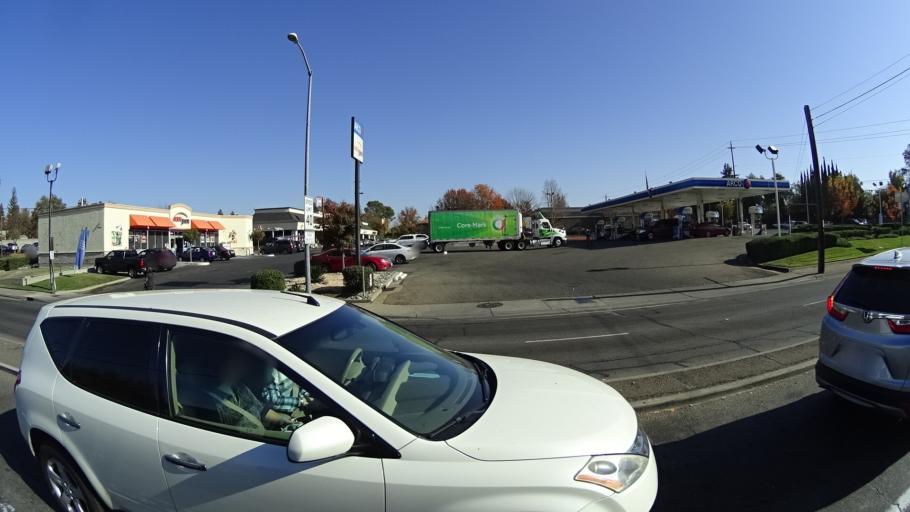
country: US
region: California
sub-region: Sacramento County
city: Fair Oaks
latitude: 38.6643
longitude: -121.2923
